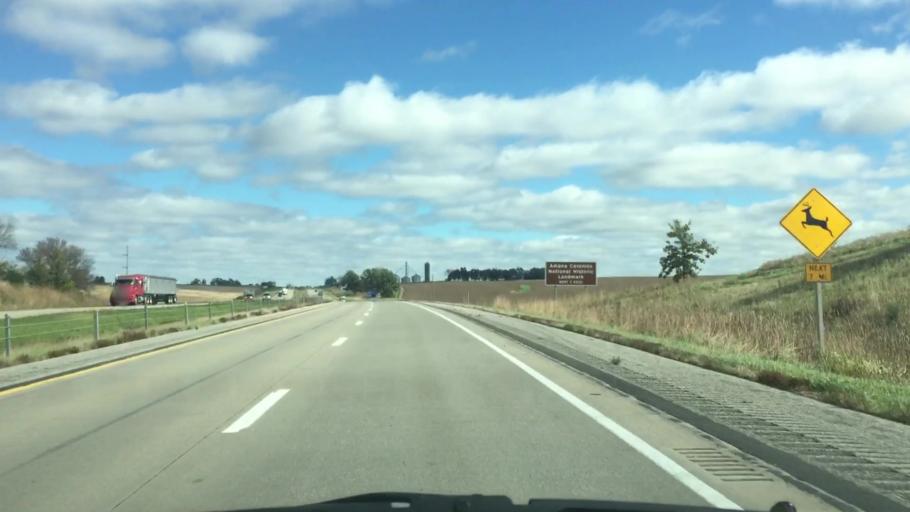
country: US
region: Iowa
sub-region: Iowa County
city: Williamsburg
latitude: 41.6872
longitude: -92.0498
